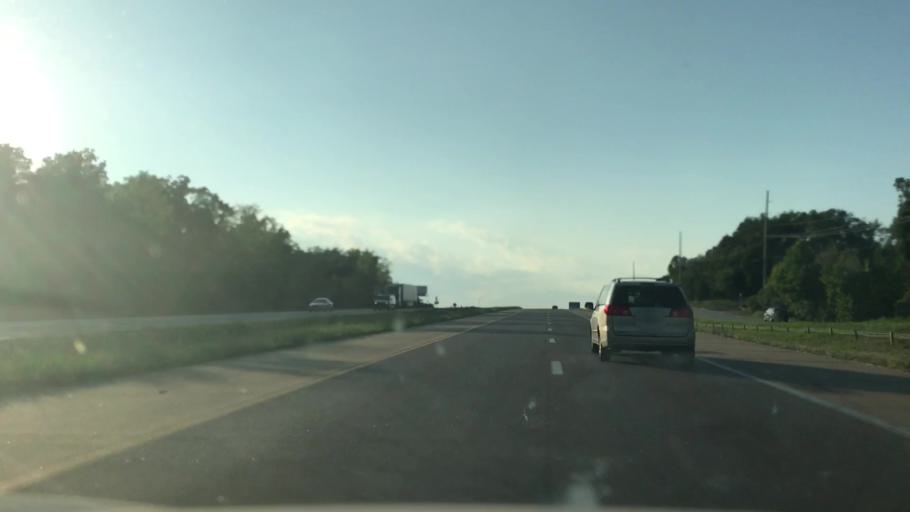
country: US
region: Missouri
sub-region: Saint Charles County
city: Dardenne Prairie
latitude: 38.7415
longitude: -90.7463
